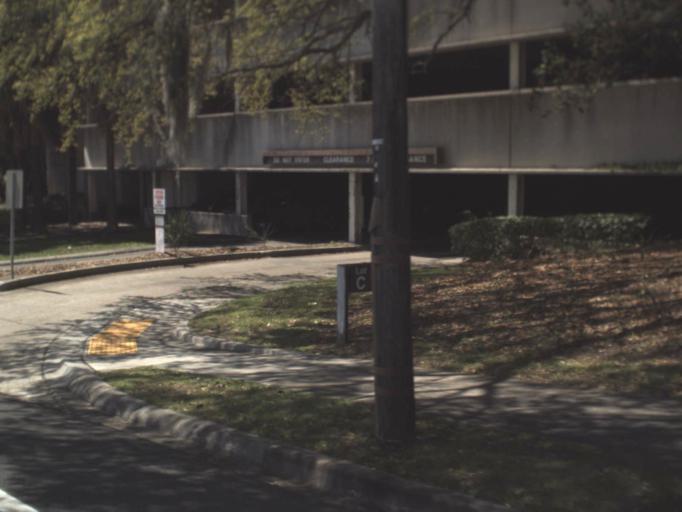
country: US
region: Florida
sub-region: Leon County
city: Tallahassee
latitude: 30.4336
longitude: -84.2807
